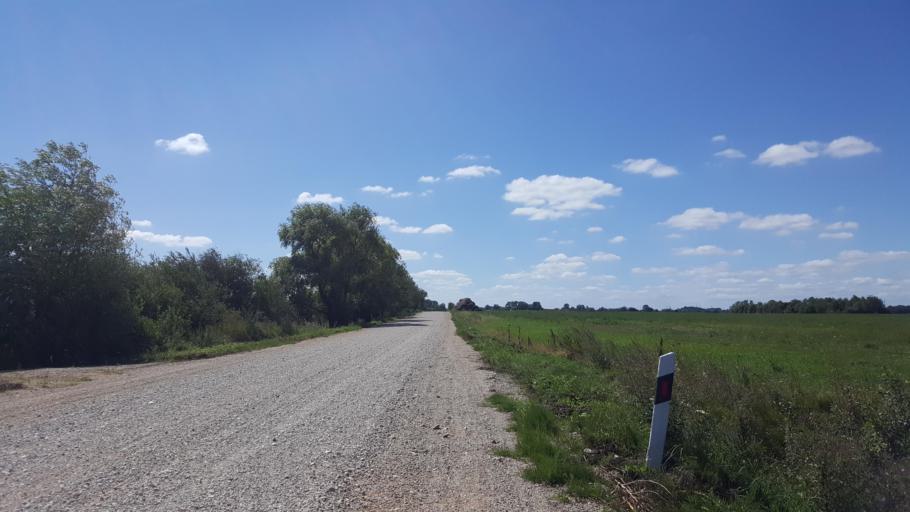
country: BY
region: Brest
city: Horad Kobryn
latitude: 52.3116
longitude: 24.3859
